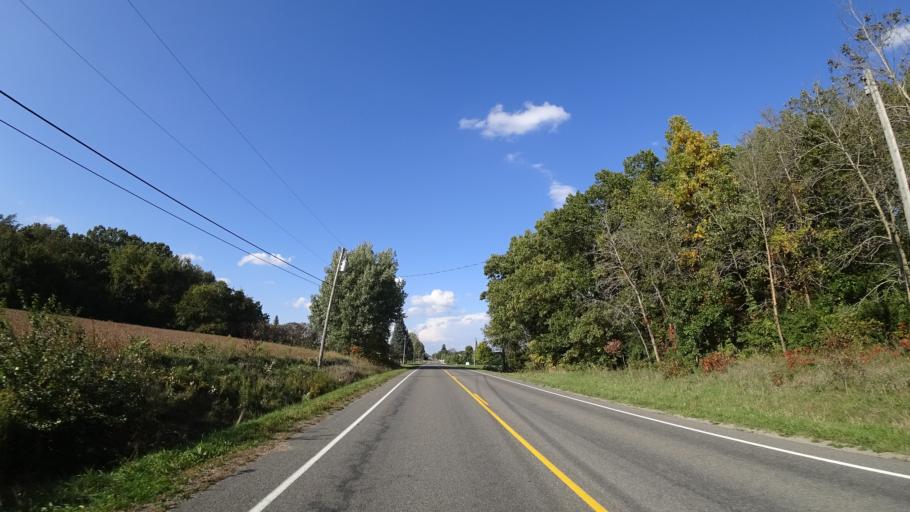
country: US
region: Michigan
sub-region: Saint Joseph County
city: Centreville
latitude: 41.8601
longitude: -85.5065
